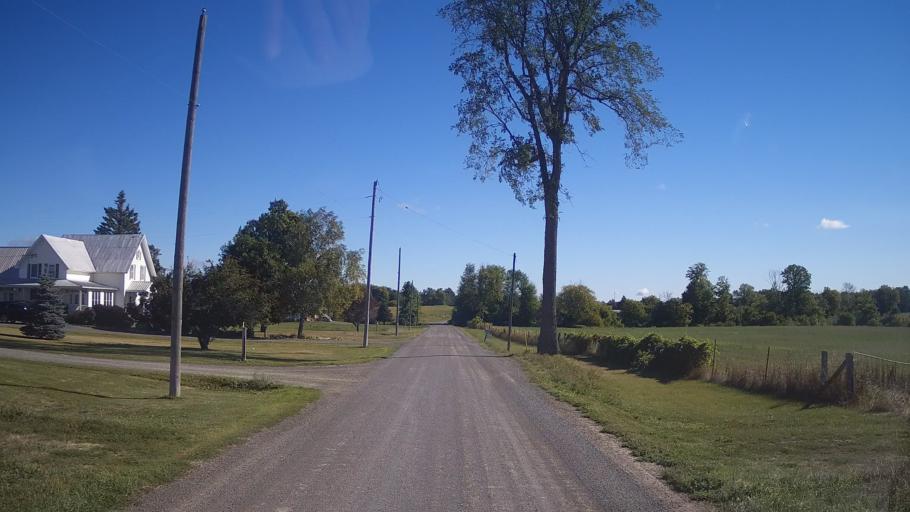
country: CA
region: Ontario
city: Prescott
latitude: 44.9780
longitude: -75.5481
